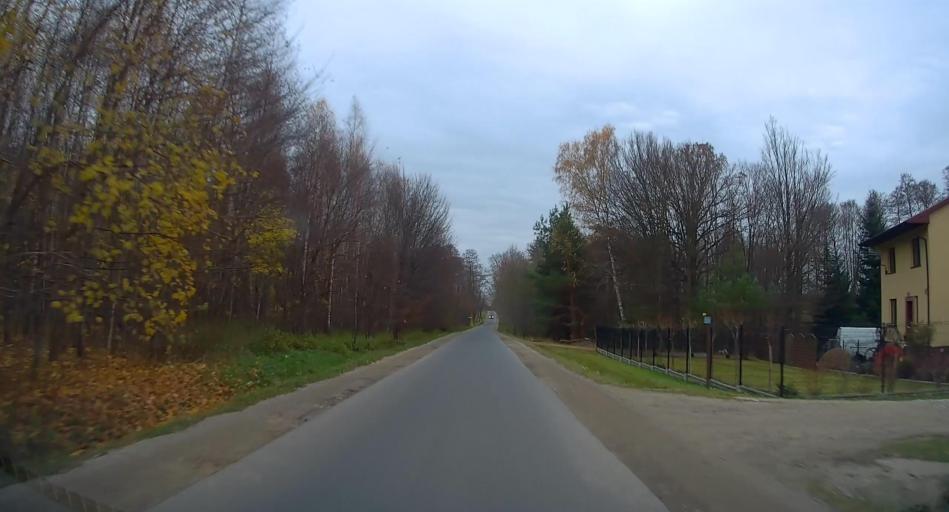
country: PL
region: Lodz Voivodeship
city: Zabia Wola
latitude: 51.9999
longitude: 20.6583
